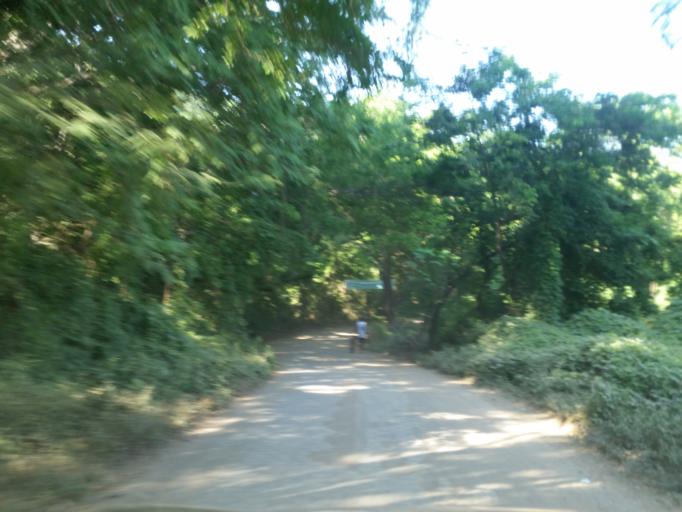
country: NI
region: Masaya
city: Catarina
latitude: 11.9334
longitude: -86.0550
